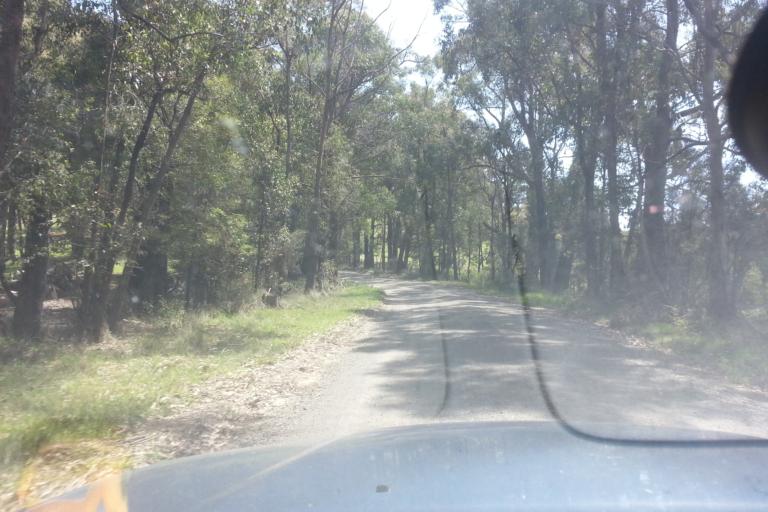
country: AU
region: Victoria
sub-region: Cardinia
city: Pakenham Upper
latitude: -37.9827
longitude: 145.4943
